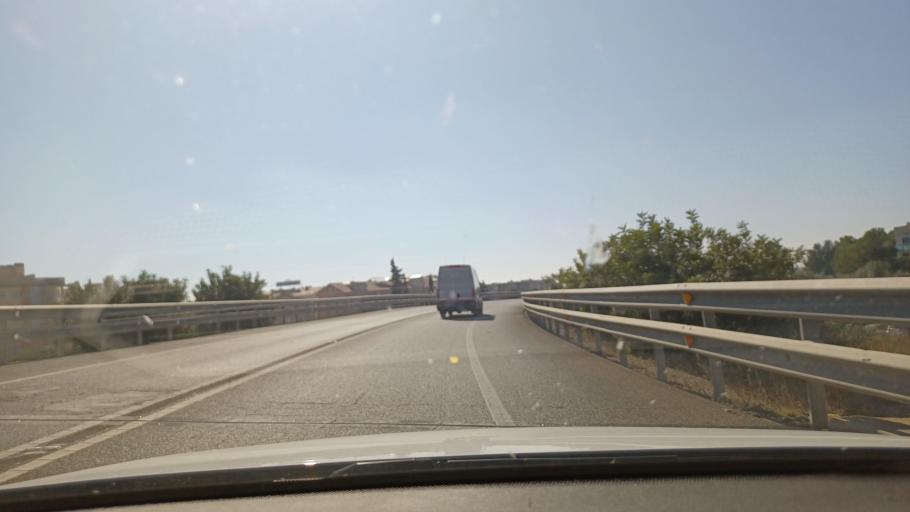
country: ES
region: Catalonia
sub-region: Provincia de Tarragona
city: L'Ampolla
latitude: 40.8114
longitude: 0.7046
